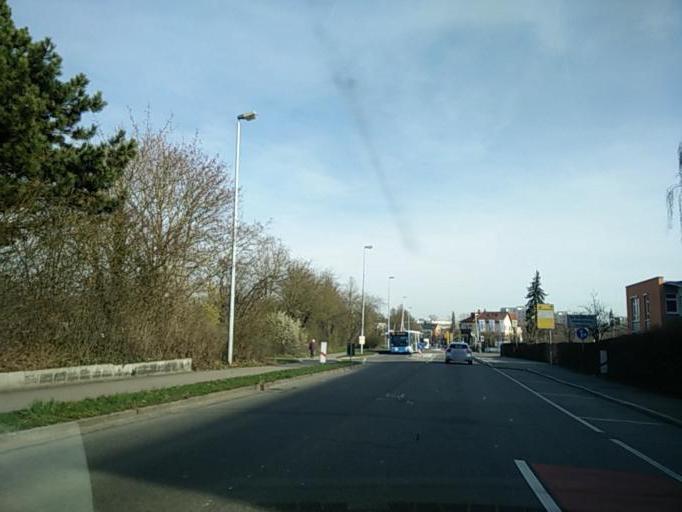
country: DE
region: Baden-Wuerttemberg
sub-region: Regierungsbezirk Stuttgart
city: Boeblingen
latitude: 48.6761
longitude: 9.0113
